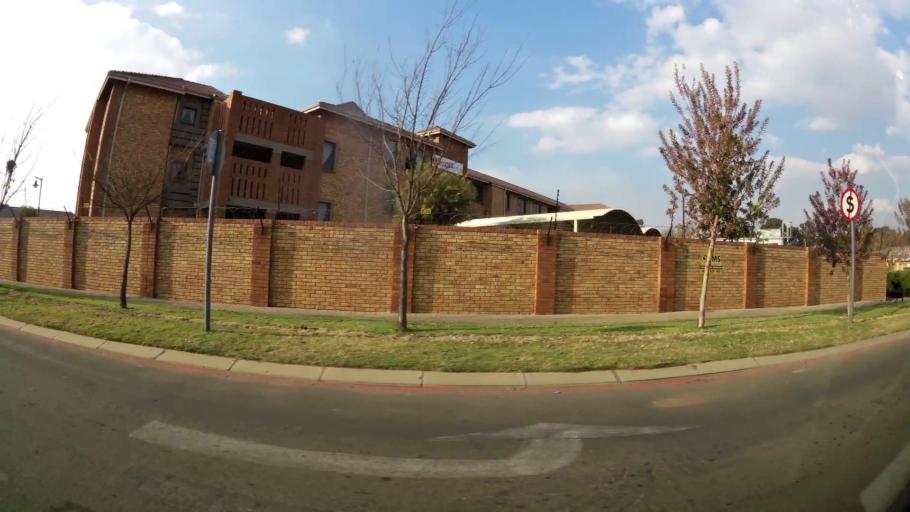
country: ZA
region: Gauteng
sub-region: Ekurhuleni Metropolitan Municipality
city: Benoni
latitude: -26.1172
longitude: 28.2821
